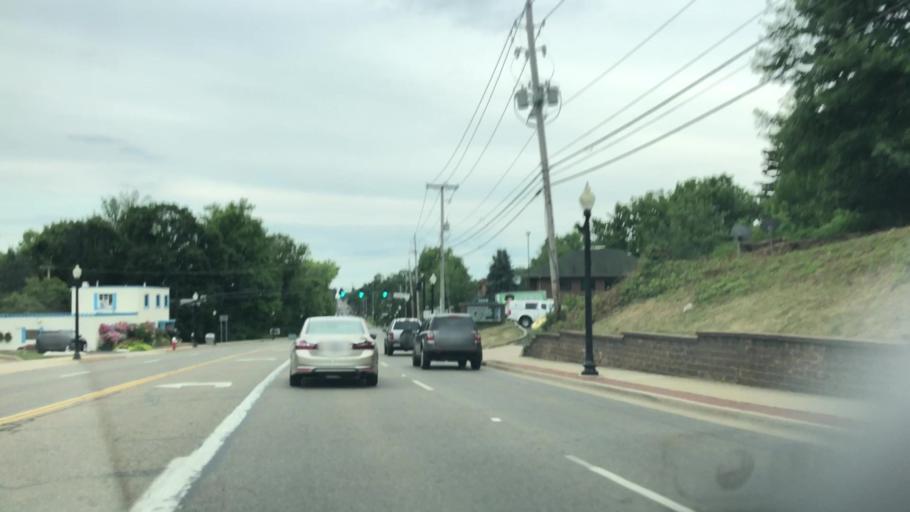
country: US
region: Ohio
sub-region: Stark County
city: North Canton
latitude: 40.8619
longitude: -81.3959
